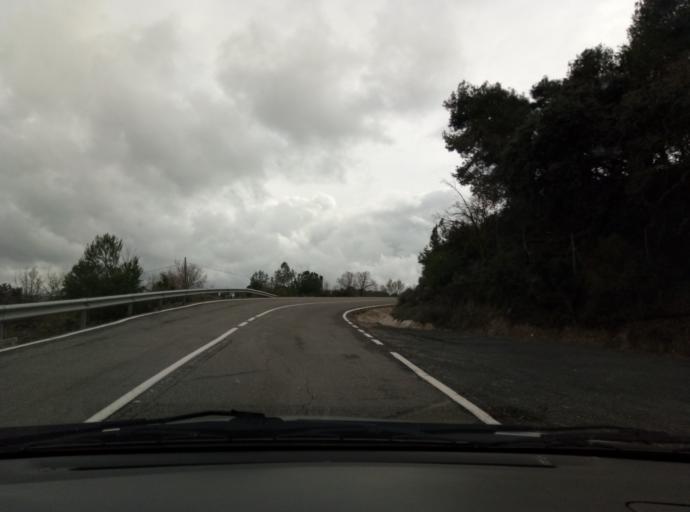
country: ES
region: Catalonia
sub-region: Provincia de Tarragona
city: Santa Coloma de Queralt
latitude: 41.5959
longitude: 1.3470
